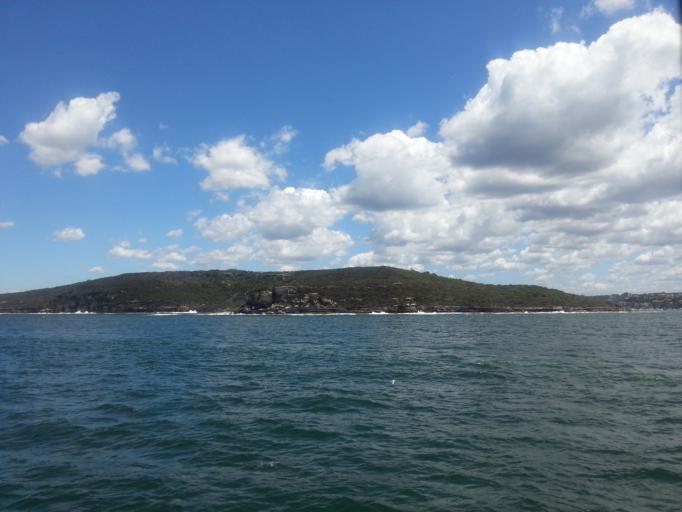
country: AU
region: New South Wales
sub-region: Manly Vale
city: Manly
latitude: -33.8146
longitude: 151.2796
